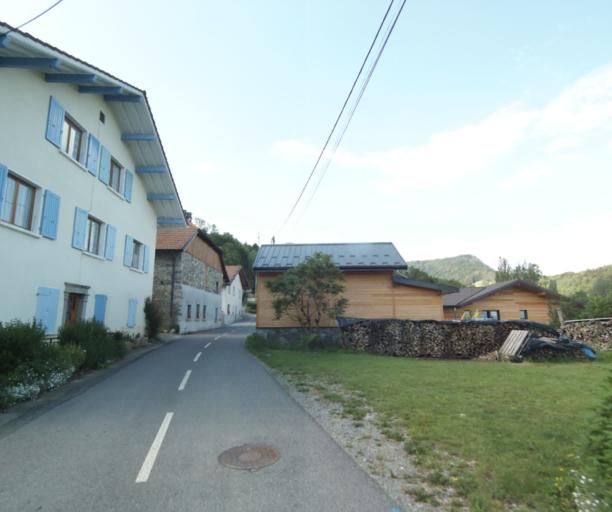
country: FR
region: Rhone-Alpes
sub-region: Departement de la Haute-Savoie
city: Lyaud
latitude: 46.3143
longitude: 6.5098
